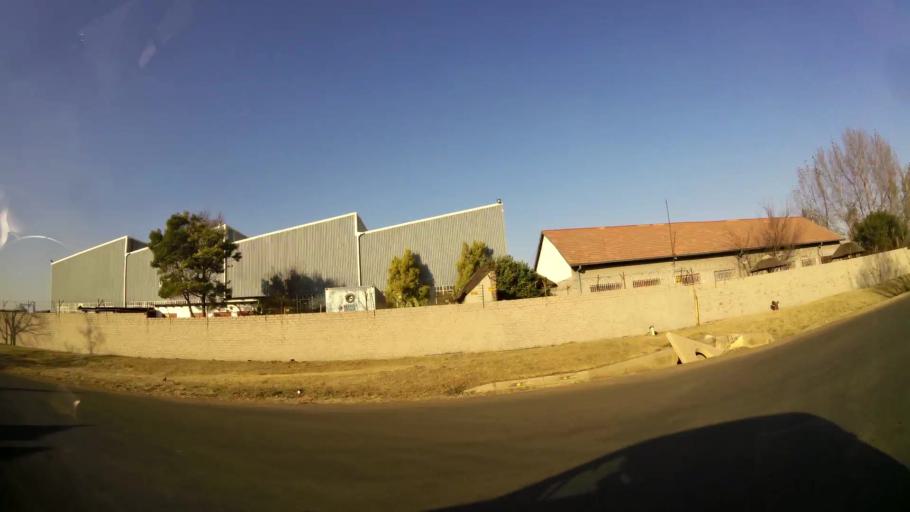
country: ZA
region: Gauteng
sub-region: West Rand District Municipality
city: Randfontein
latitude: -26.2008
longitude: 27.6835
